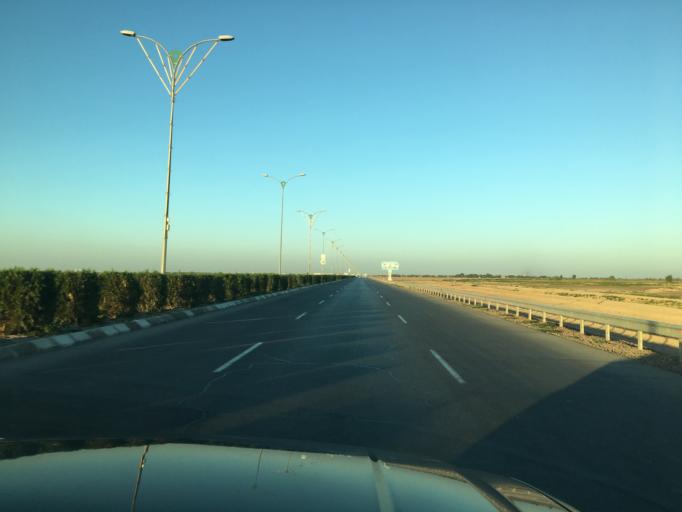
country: TM
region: Dasoguz
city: Dasoguz
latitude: 41.7787
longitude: 59.8498
